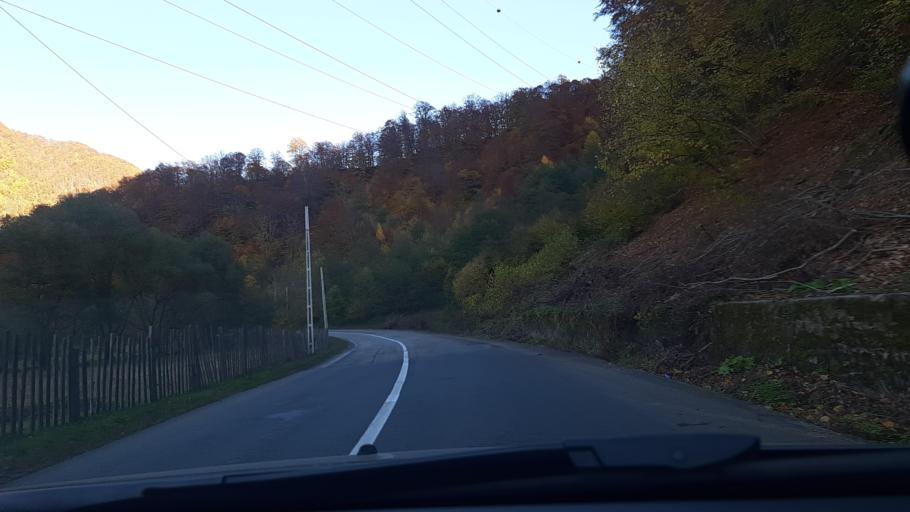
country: RO
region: Valcea
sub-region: Comuna Brezoi
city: Brezoi
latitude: 45.3472
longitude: 24.1479
